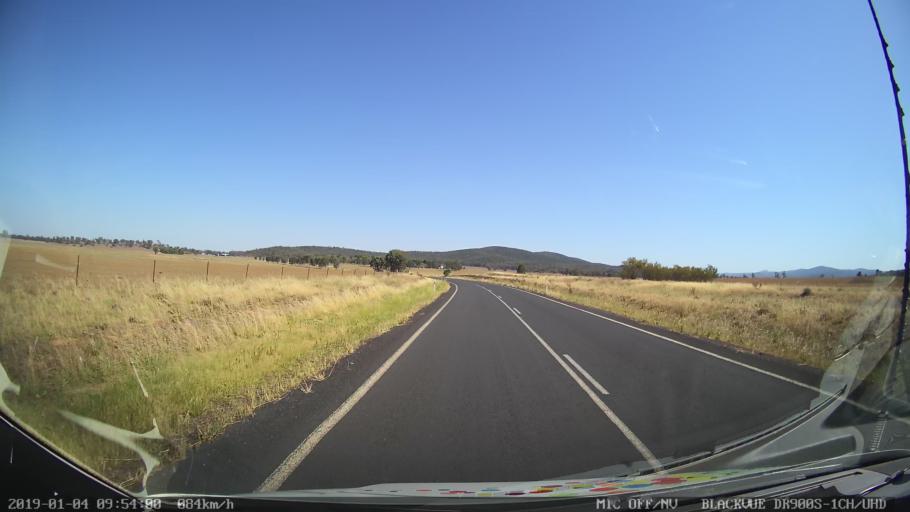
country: AU
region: New South Wales
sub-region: Cabonne
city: Canowindra
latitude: -33.5458
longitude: 148.4187
